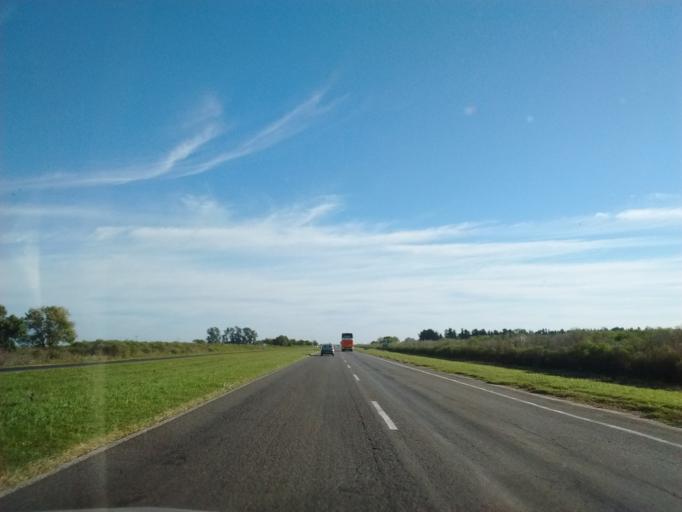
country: AR
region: Santa Fe
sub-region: Departamento de San Lorenzo
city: San Lorenzo
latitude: -32.5575
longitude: -60.8834
